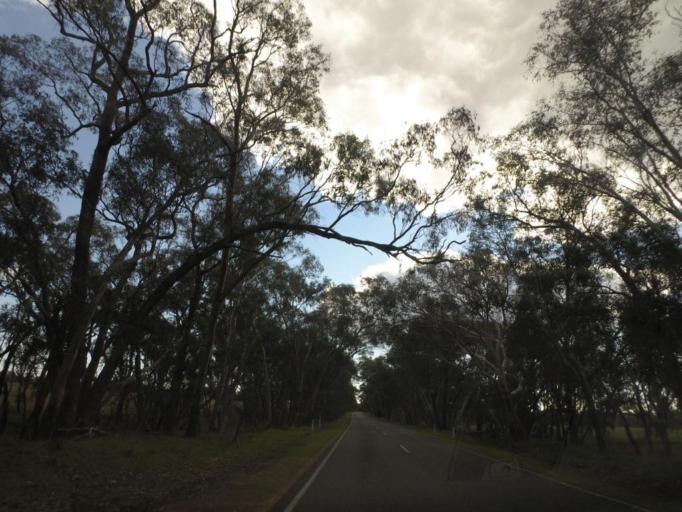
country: AU
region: New South Wales
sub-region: Corowa Shire
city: Howlong
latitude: -36.1869
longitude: 146.6105
